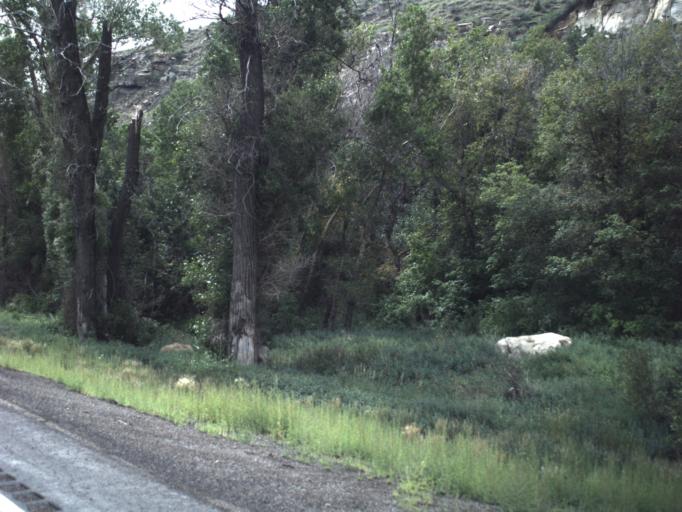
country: US
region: Utah
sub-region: Carbon County
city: Helper
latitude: 39.7767
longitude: -110.9150
